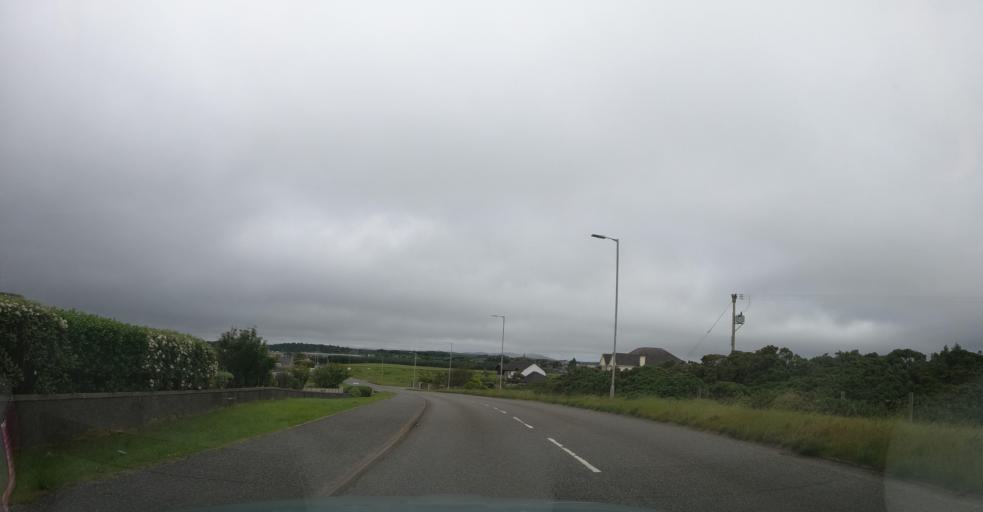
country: GB
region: Scotland
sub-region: Eilean Siar
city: Stornoway
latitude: 58.2080
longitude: -6.3615
